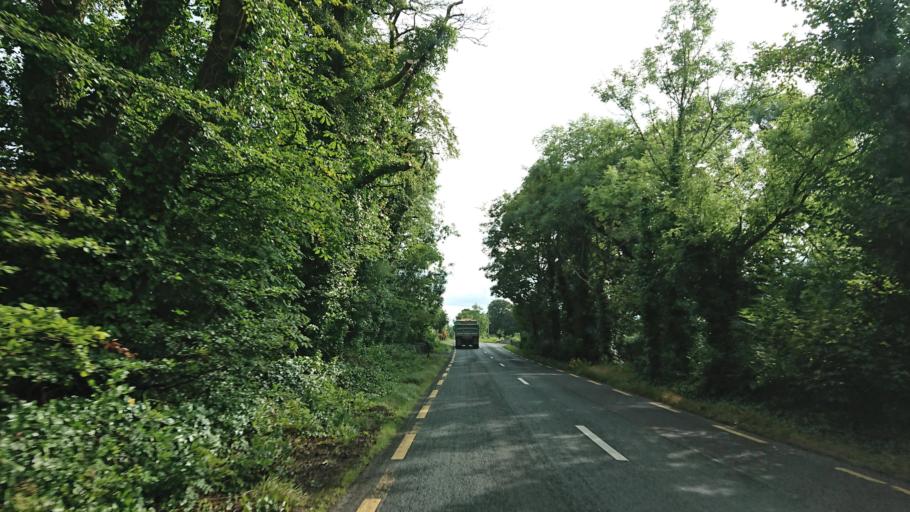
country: IE
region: Connaught
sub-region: County Leitrim
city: Carrick-on-Shannon
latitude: 53.9662
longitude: -8.0709
